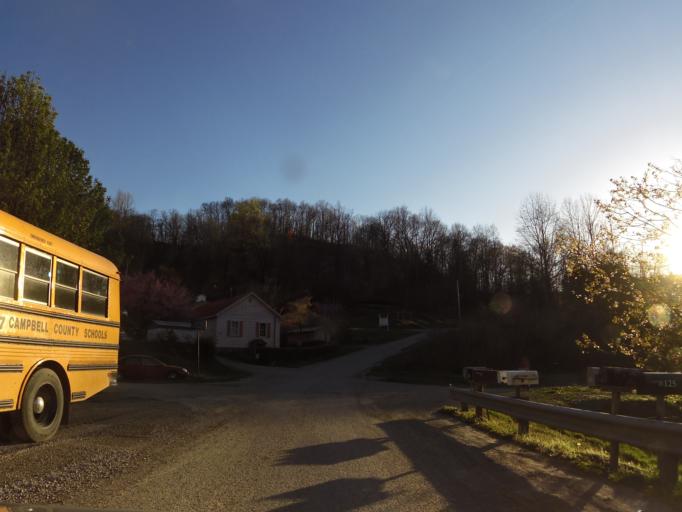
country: US
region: Tennessee
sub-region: Campbell County
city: Caryville
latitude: 36.2379
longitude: -84.3307
